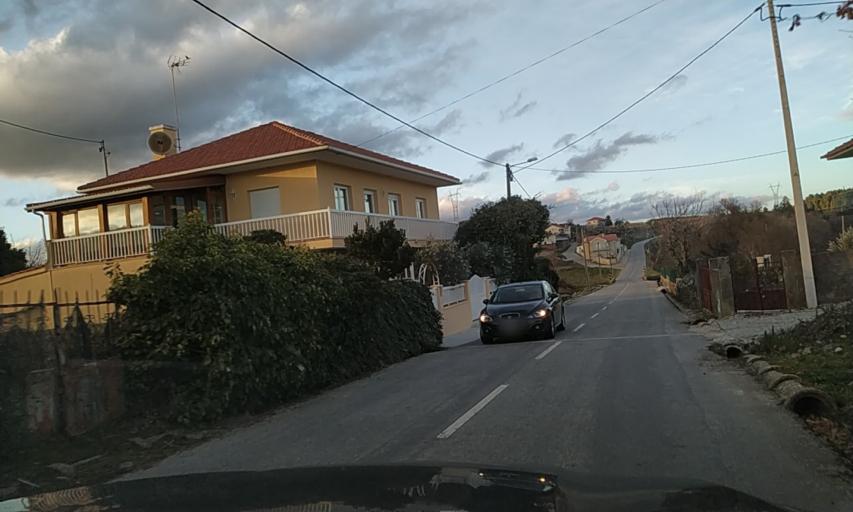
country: PT
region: Braganca
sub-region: Carrazeda de Ansiaes
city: Carrazeda de Anciaes
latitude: 41.2125
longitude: -7.3192
